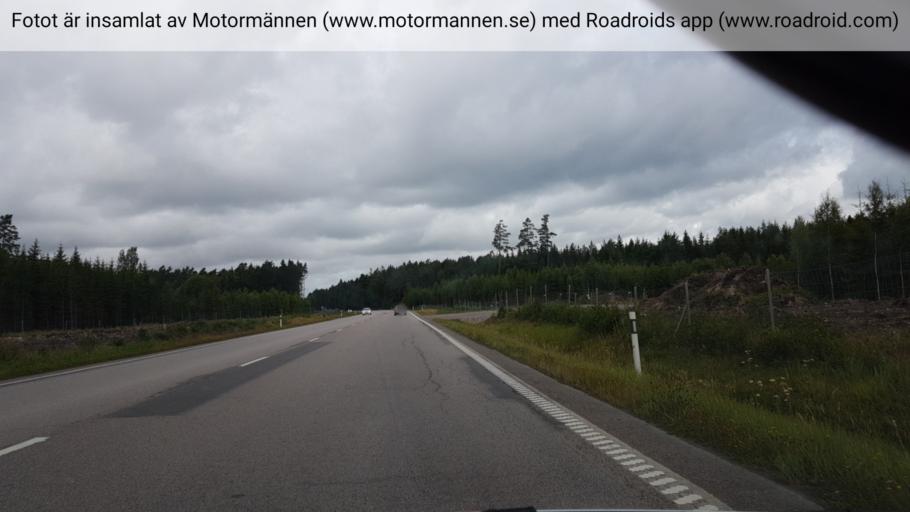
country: SE
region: Vaestra Goetaland
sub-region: Lidkopings Kommun
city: Lidkoping
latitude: 58.4782
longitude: 13.2033
